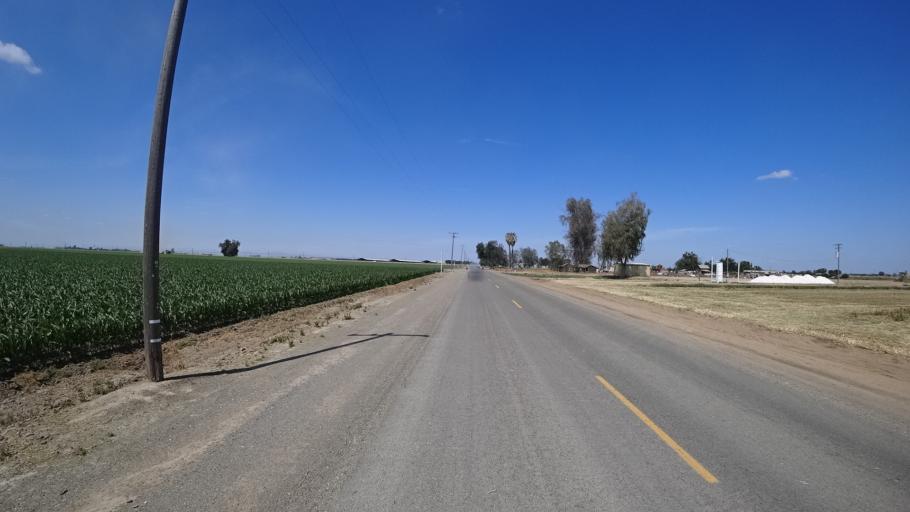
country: US
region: California
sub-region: Kings County
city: Home Garden
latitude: 36.2694
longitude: -119.6131
